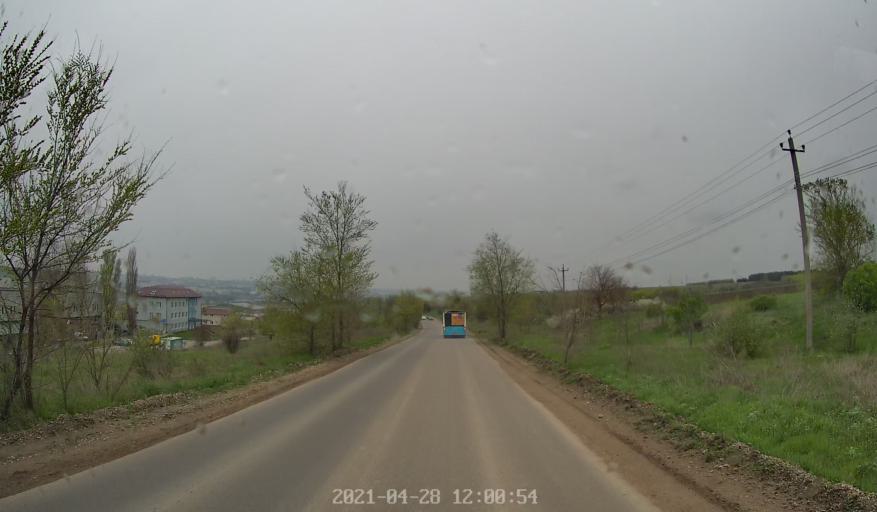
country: MD
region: Chisinau
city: Chisinau
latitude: 46.9876
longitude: 28.9250
